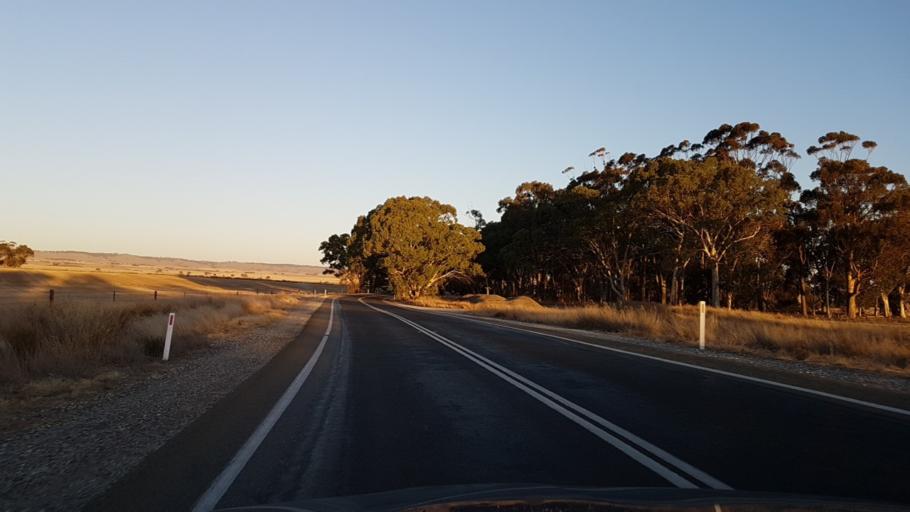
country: AU
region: South Australia
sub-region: Light
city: Kapunda
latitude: -34.2284
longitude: 138.7351
